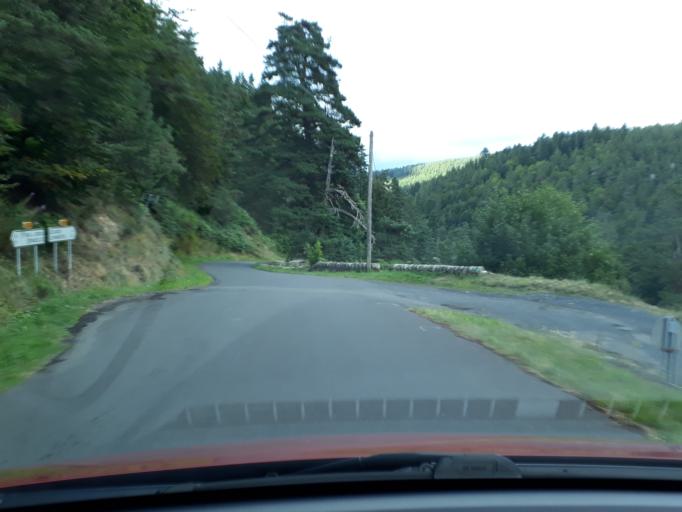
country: FR
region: Auvergne
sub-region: Departement de la Haute-Loire
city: Le Monastier-sur-Gazeille
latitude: 44.8219
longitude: 3.9432
